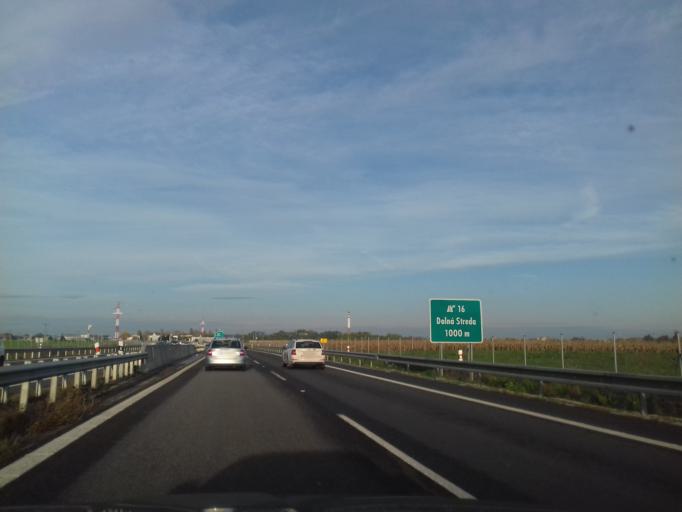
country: SK
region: Trnavsky
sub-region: Okres Galanta
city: Galanta
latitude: 48.2572
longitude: 17.7634
